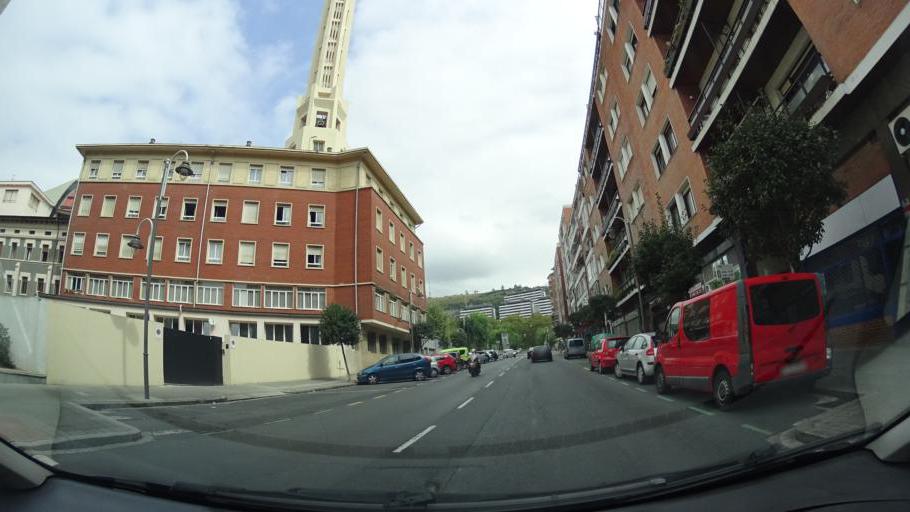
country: ES
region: Basque Country
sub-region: Bizkaia
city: Bilbao
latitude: 43.2705
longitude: -2.9509
